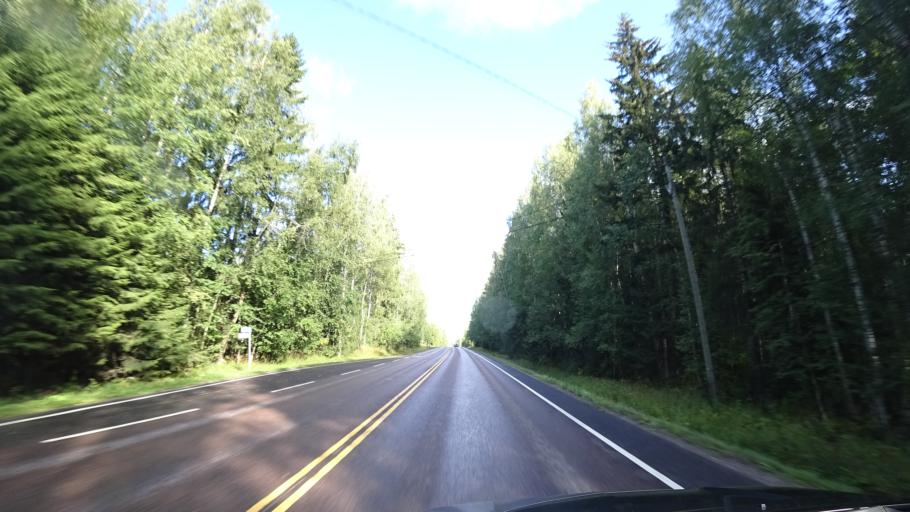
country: FI
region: Uusimaa
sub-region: Helsinki
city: Tuusula
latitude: 60.4956
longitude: 24.9379
